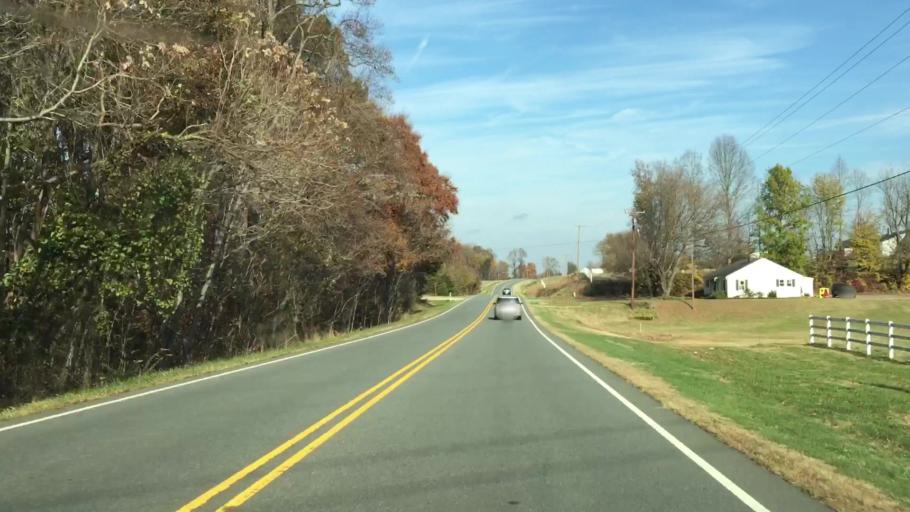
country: US
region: North Carolina
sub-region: Forsyth County
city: Walkertown
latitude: 36.1874
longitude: -80.1102
